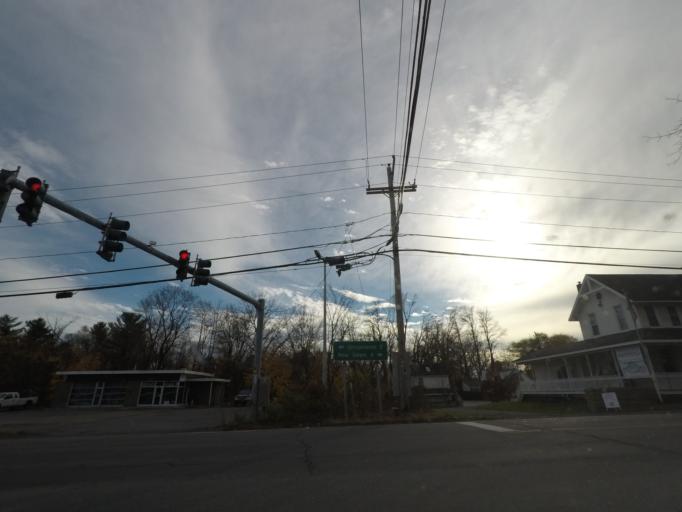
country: US
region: New York
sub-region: Albany County
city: Voorheesville
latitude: 42.6324
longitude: -73.9025
